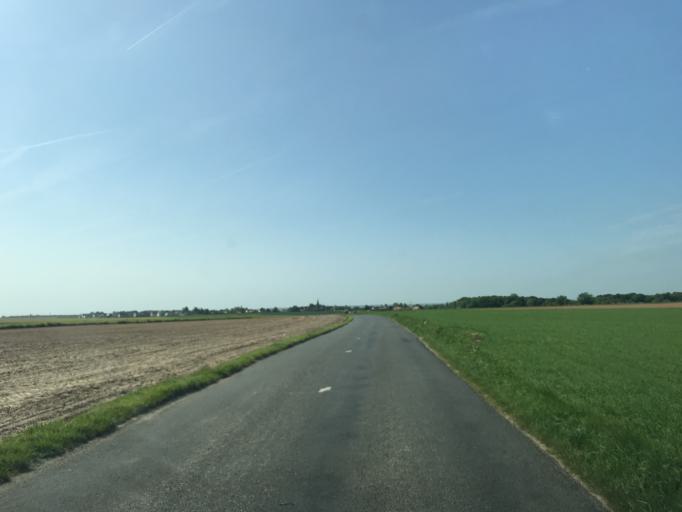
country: FR
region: Haute-Normandie
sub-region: Departement de la Seine-Maritime
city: Belbeuf
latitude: 49.3758
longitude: 1.1611
